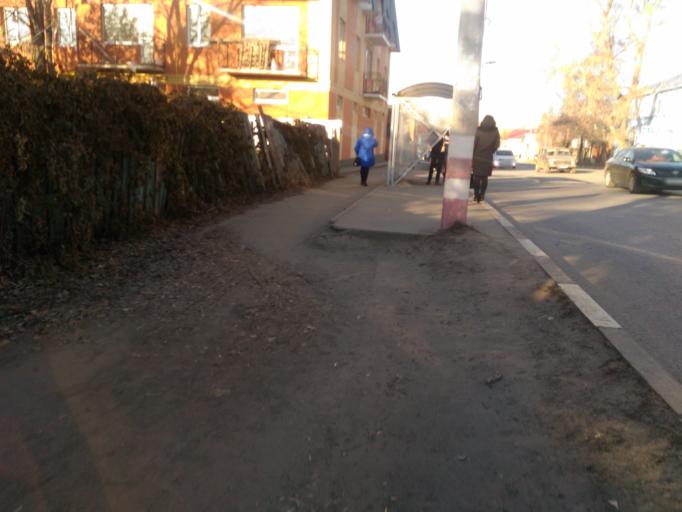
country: RU
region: Ulyanovsk
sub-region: Ulyanovskiy Rayon
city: Ulyanovsk
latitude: 54.3110
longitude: 48.3786
